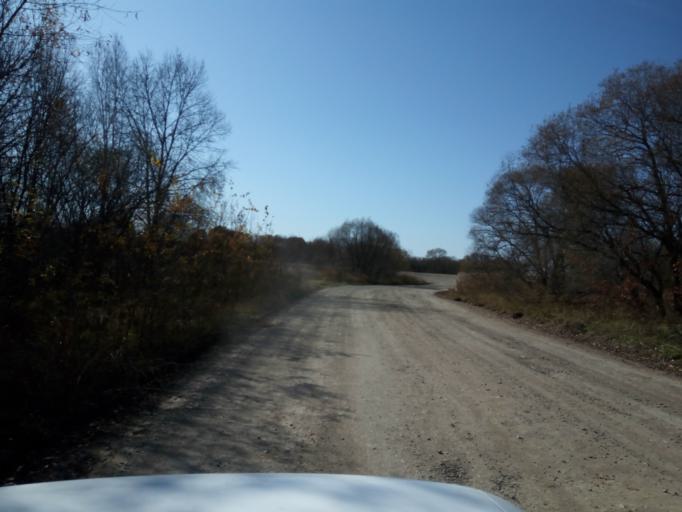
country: RU
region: Primorskiy
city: Dal'nerechensk
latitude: 45.9187
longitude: 133.7764
